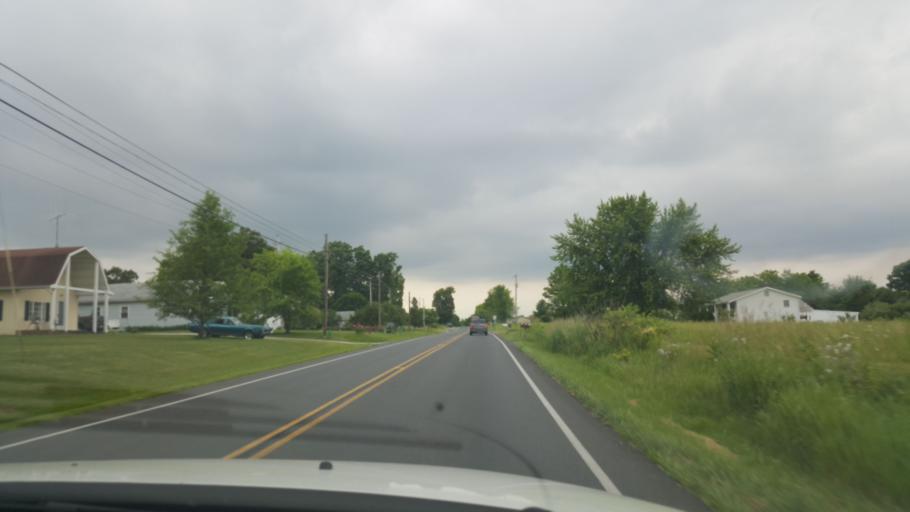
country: US
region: Pennsylvania
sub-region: Adams County
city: Lake Meade
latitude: 39.9489
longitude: -77.1040
